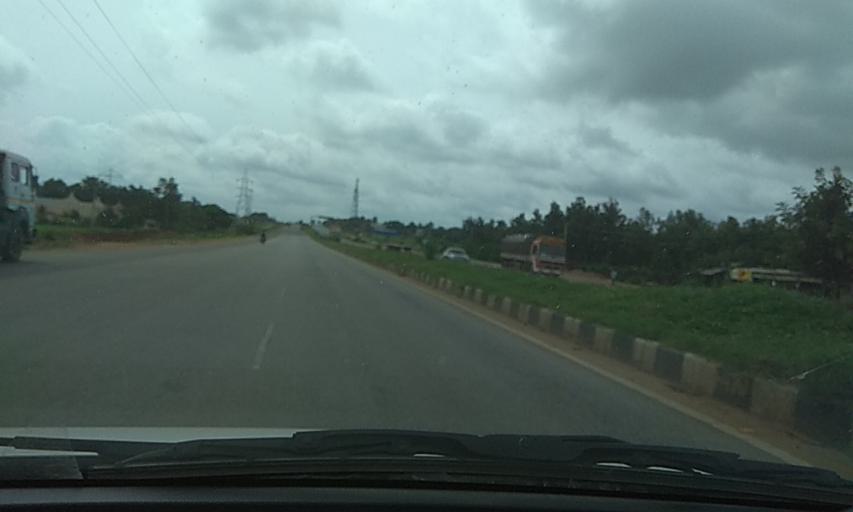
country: IN
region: Karnataka
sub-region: Davanagere
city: Mayakonda
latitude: 14.4145
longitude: 75.9855
